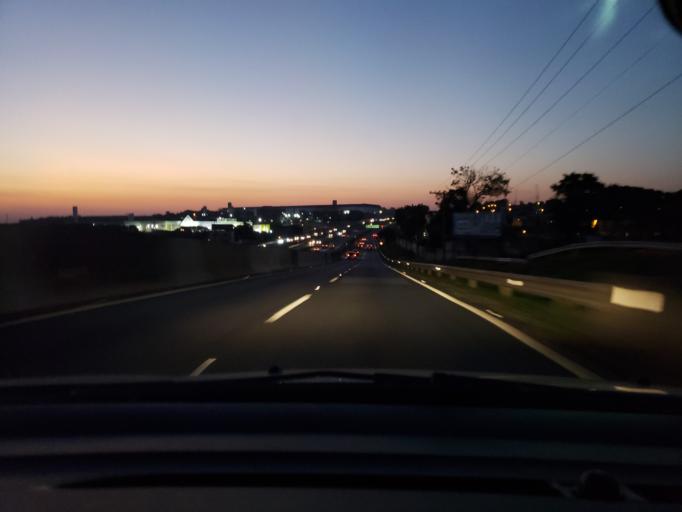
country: BR
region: Sao Paulo
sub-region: Campinas
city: Campinas
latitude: -22.9070
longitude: -47.1050
